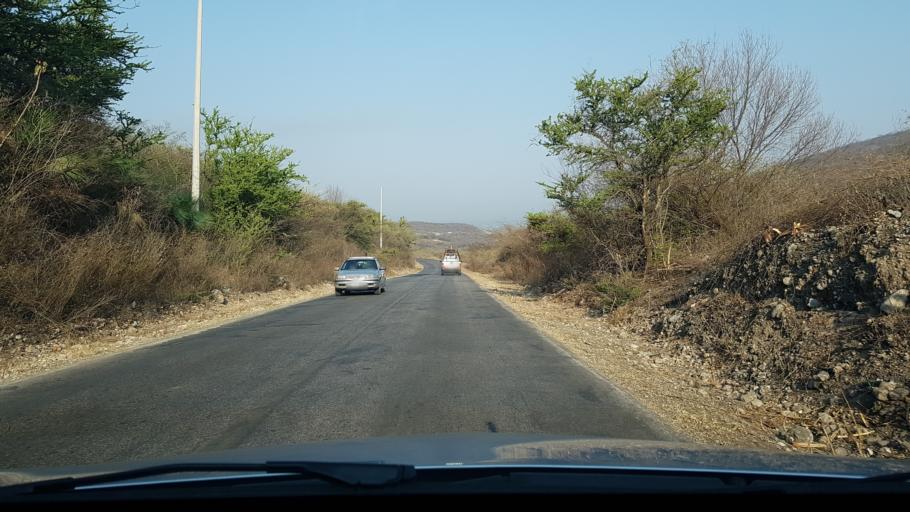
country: MX
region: Morelos
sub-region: Tlaltizapan de Zapata
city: Colonia Palo Prieto (Chipitongo)
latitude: 18.6753
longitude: -99.0630
